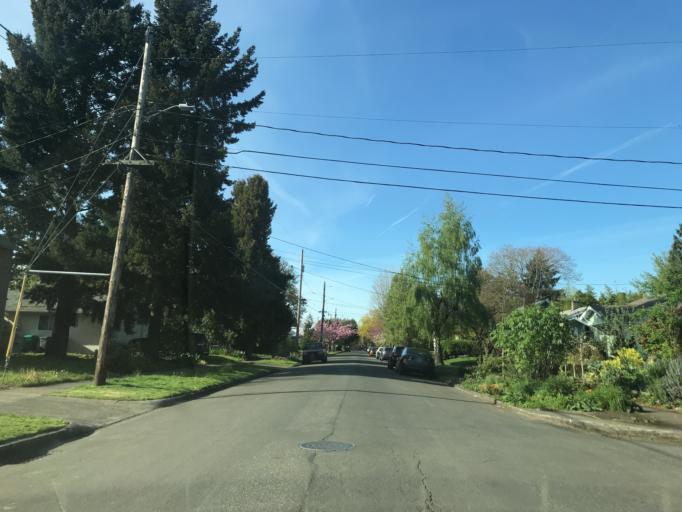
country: US
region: Oregon
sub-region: Multnomah County
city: Lents
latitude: 45.4982
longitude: -122.6019
